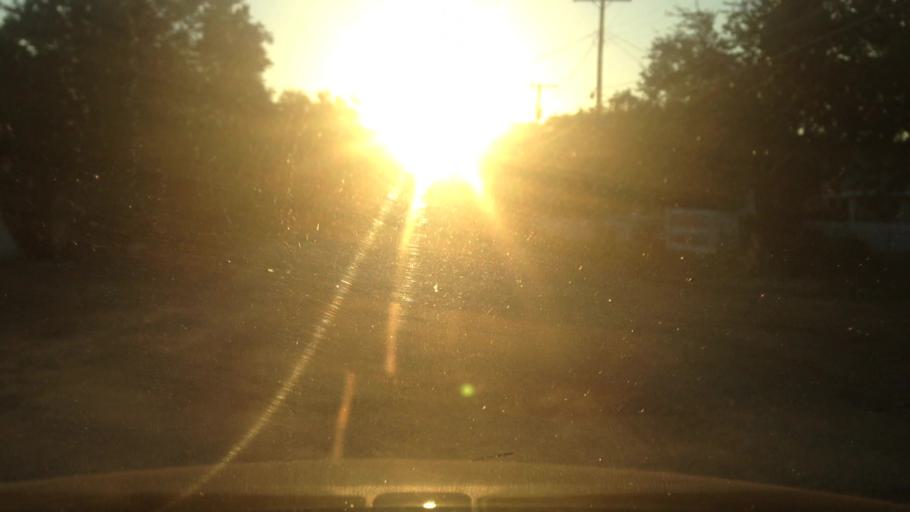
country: US
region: Texas
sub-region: Tarrant County
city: Haltom City
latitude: 32.7969
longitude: -97.3024
